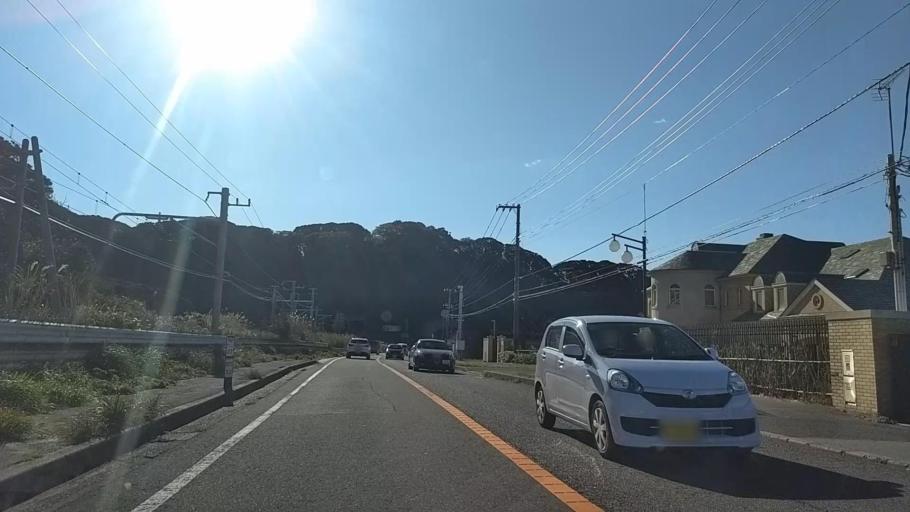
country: JP
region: Chiba
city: Futtsu
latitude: 35.1827
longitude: 139.8190
